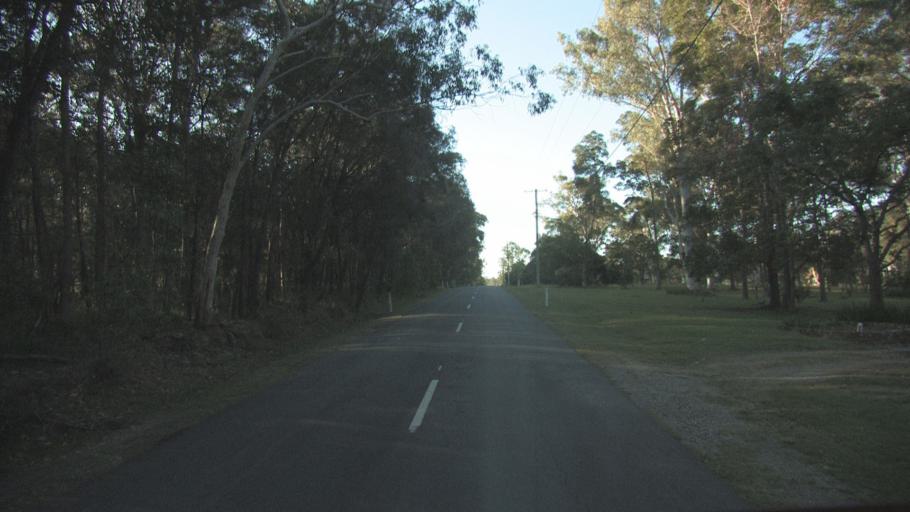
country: AU
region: Queensland
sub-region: Gold Coast
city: Yatala
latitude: -27.6810
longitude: 153.2751
